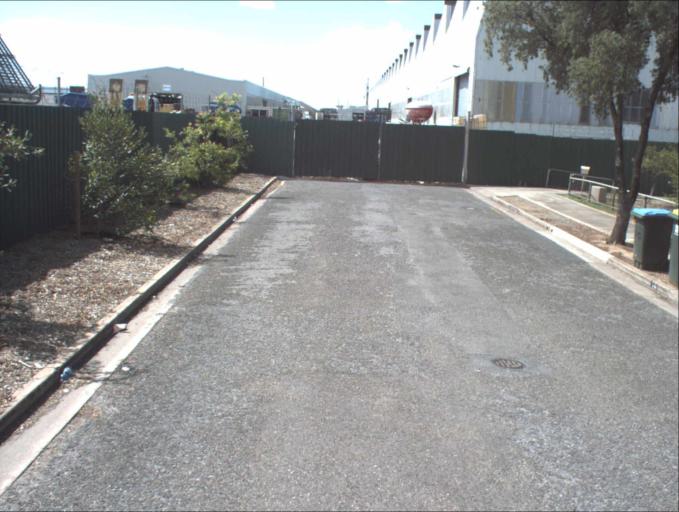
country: AU
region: South Australia
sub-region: Port Adelaide Enfield
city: Blair Athol
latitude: -34.8567
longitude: 138.5792
